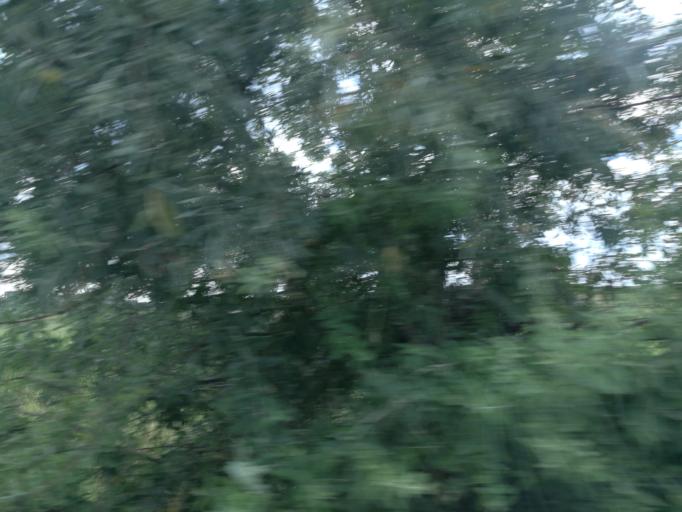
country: RO
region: Constanta
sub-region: Comuna Sacele
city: Sacele
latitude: 44.4440
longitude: 28.7496
